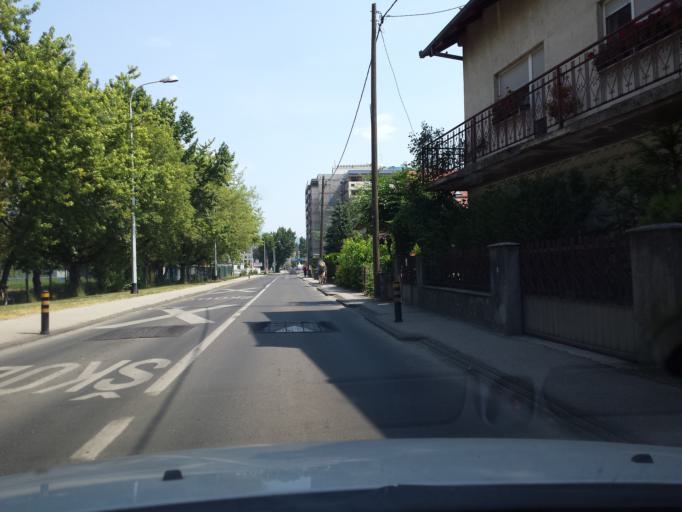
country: HR
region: Grad Zagreb
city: Jankomir
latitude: 45.7937
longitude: 15.9069
